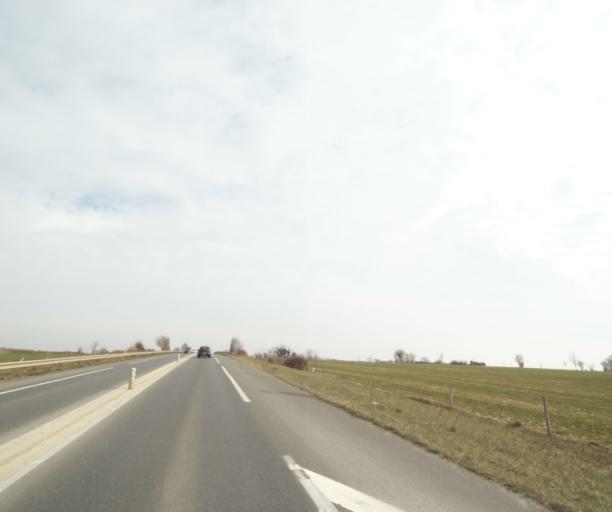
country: FR
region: Poitou-Charentes
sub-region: Departement des Deux-Sevres
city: Aiffres
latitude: 46.3060
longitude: -0.4317
